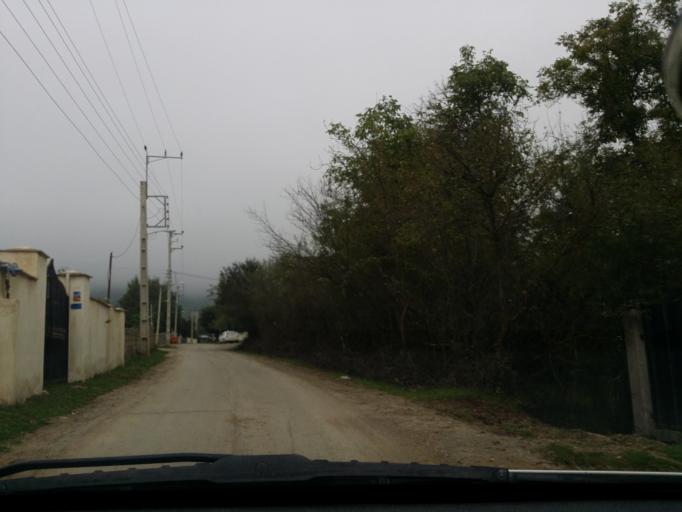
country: IR
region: Mazandaran
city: Chalus
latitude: 36.5119
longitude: 51.2262
